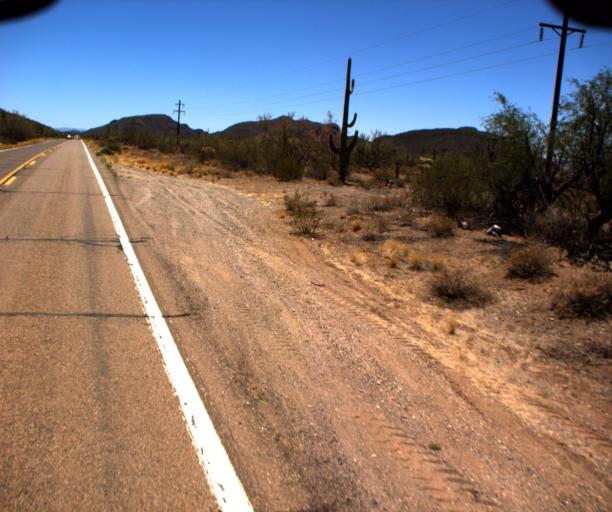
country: US
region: Arizona
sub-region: Pima County
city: Sells
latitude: 31.9796
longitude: -111.9683
